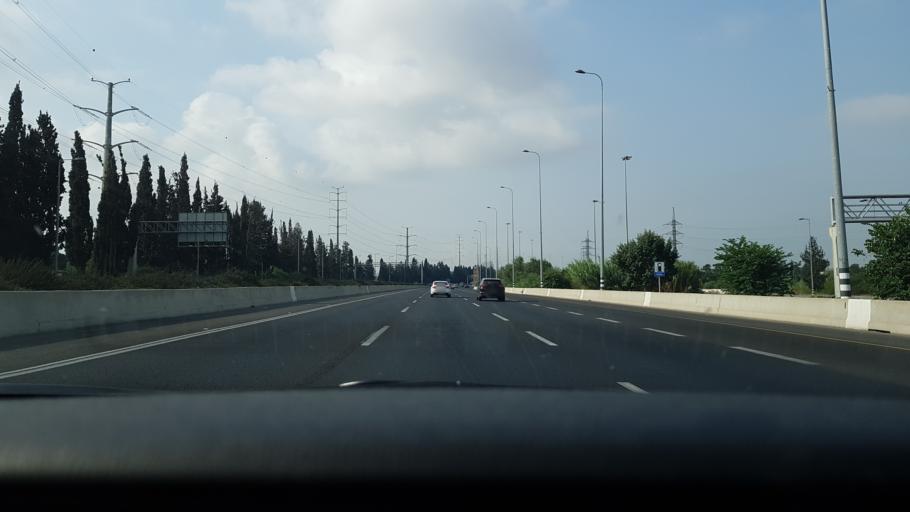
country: IL
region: Central District
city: Bet Dagan
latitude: 32.0051
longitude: 34.8106
